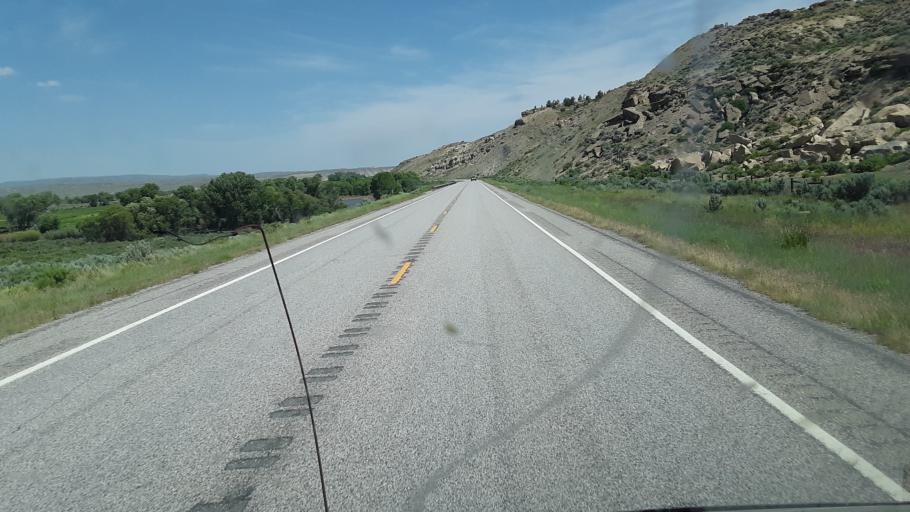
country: US
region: Montana
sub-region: Carbon County
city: Red Lodge
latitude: 45.0117
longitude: -109.0540
